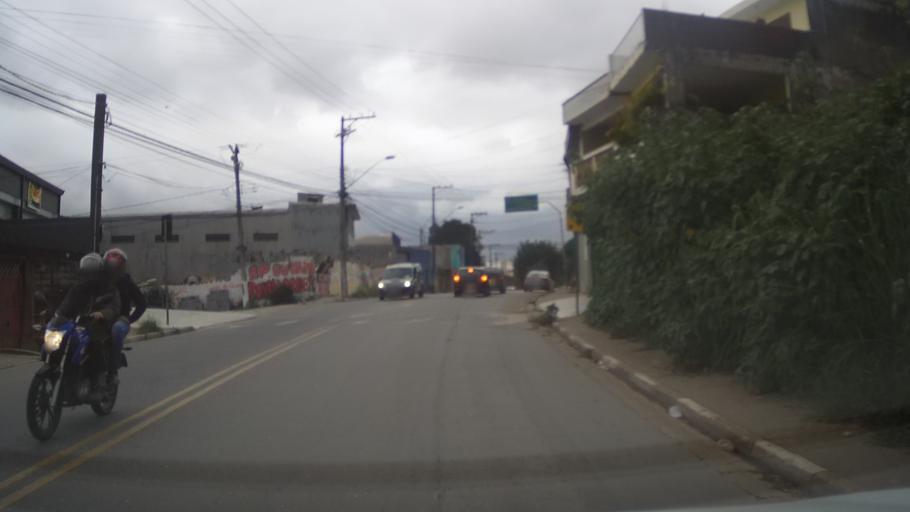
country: BR
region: Sao Paulo
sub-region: Guarulhos
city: Guarulhos
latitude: -23.4099
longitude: -46.4437
